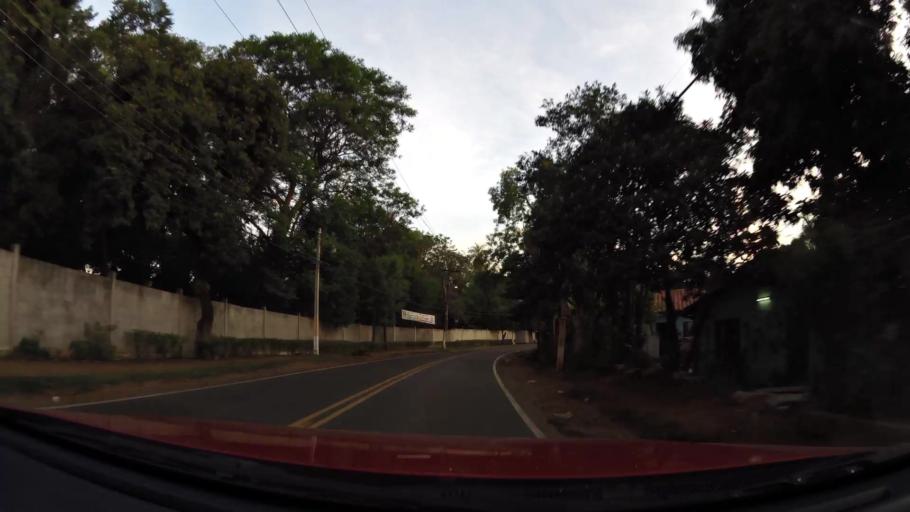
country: PY
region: Central
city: San Lorenzo
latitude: -25.3600
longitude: -57.4902
